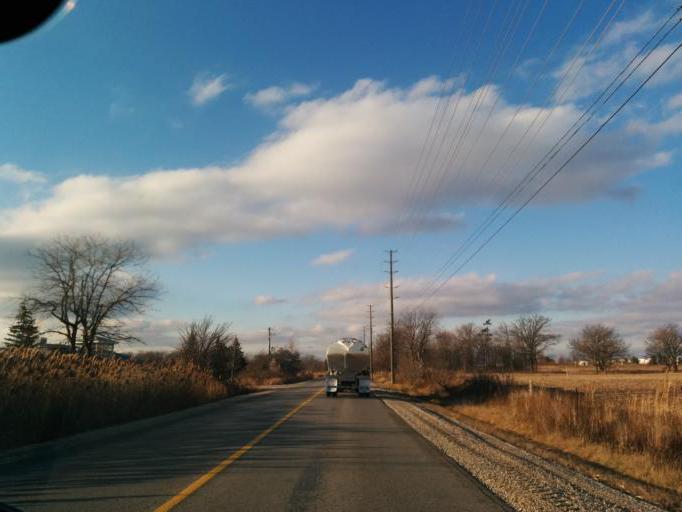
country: CA
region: Ontario
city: Oakville
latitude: 43.5149
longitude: -79.7064
